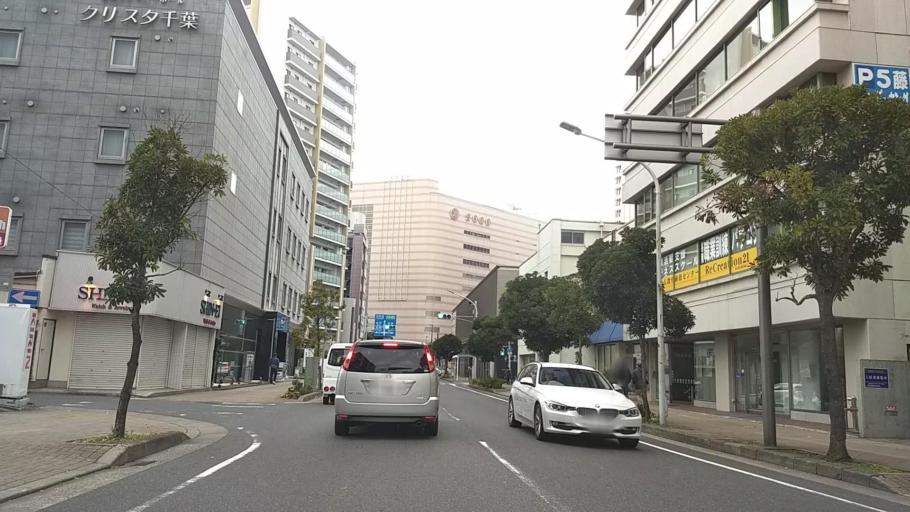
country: JP
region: Chiba
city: Chiba
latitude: 35.6088
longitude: 140.1150
